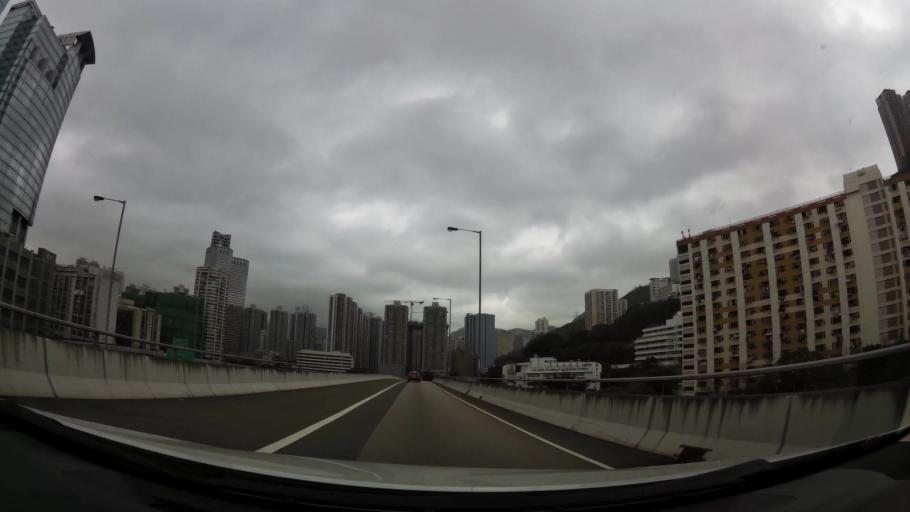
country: HK
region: Tsuen Wan
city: Tsuen Wan
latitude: 22.3517
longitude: 114.1256
